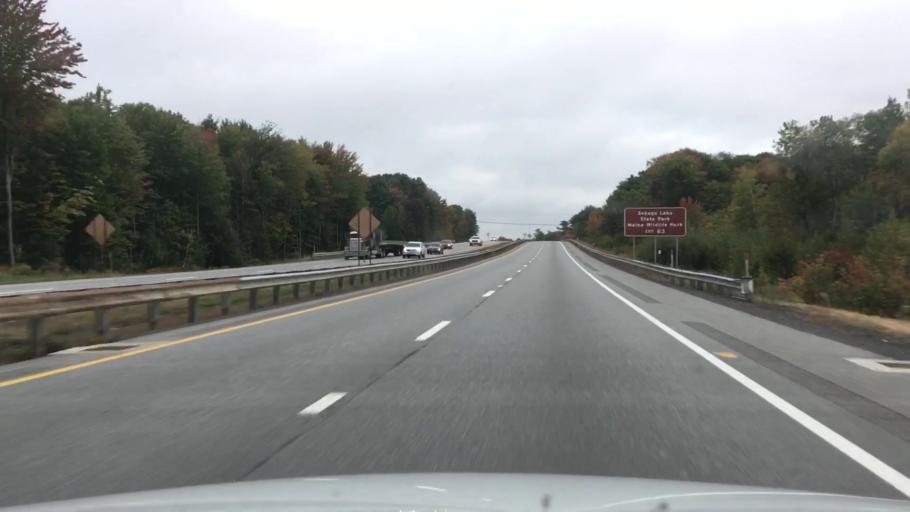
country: US
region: Maine
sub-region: Cumberland County
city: Cumberland Center
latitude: 43.8465
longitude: -70.3236
